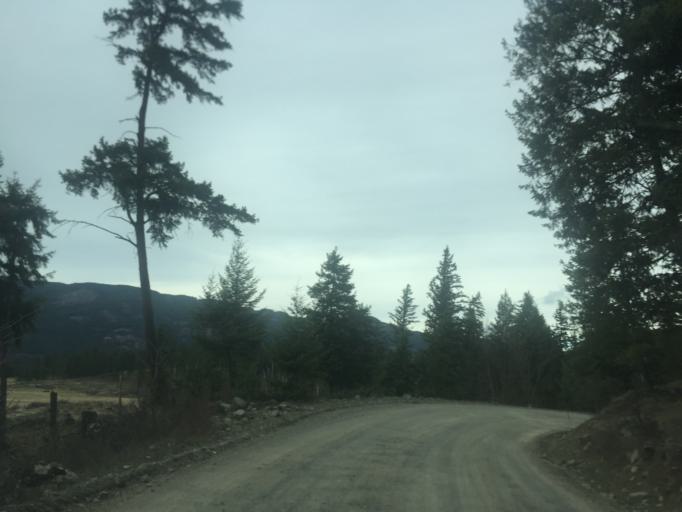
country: CA
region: British Columbia
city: Kamloops
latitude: 51.3669
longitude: -120.1546
